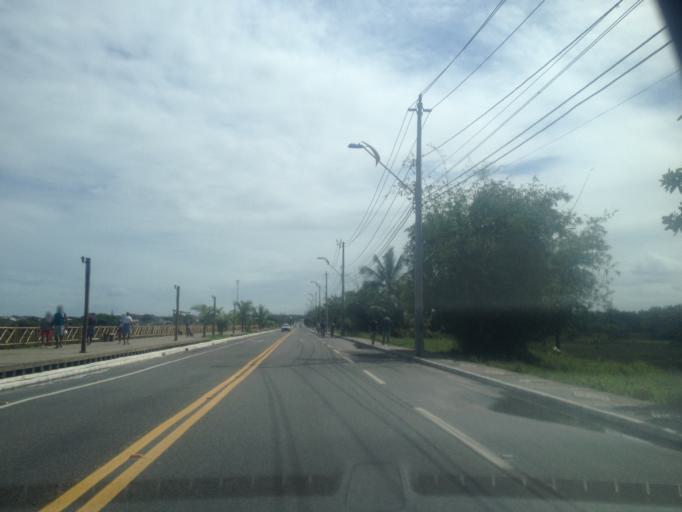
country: BR
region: Bahia
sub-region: Camacari
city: Camacari
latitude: -12.7707
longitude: -38.1796
